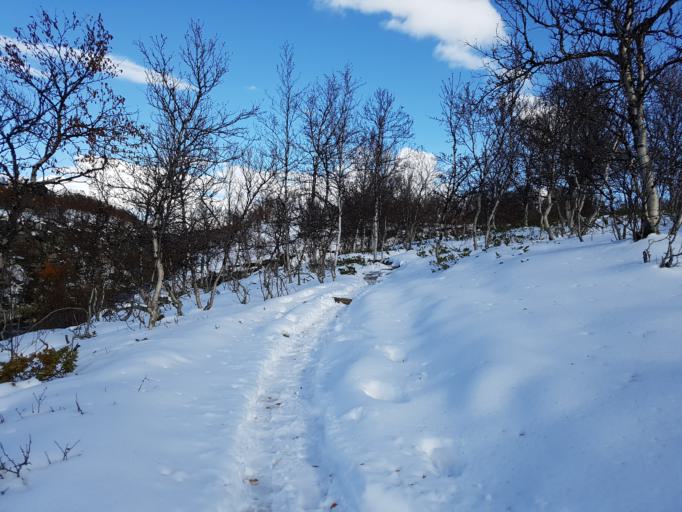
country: NO
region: Oppland
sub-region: Sel
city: Otta
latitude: 61.8282
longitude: 9.6944
